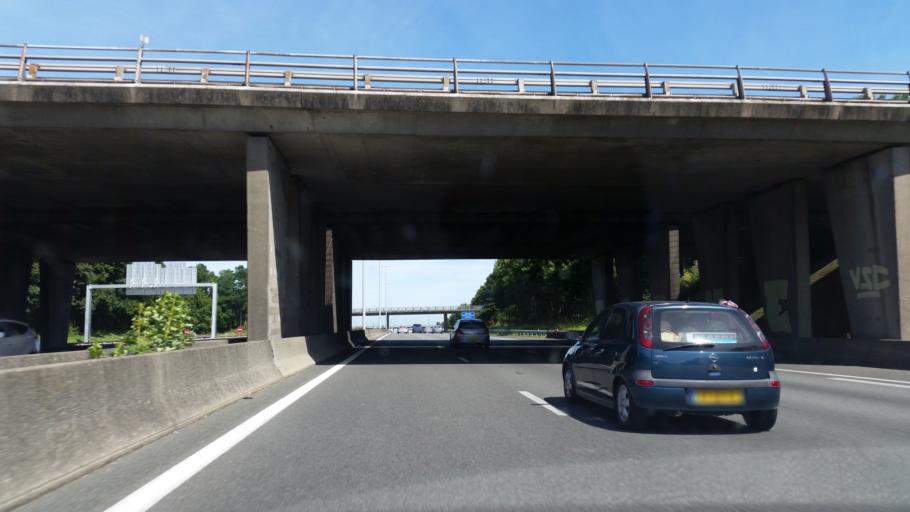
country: FR
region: Nord-Pas-de-Calais
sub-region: Departement du Pas-de-Calais
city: Roeux
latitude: 50.3143
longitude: 2.8995
